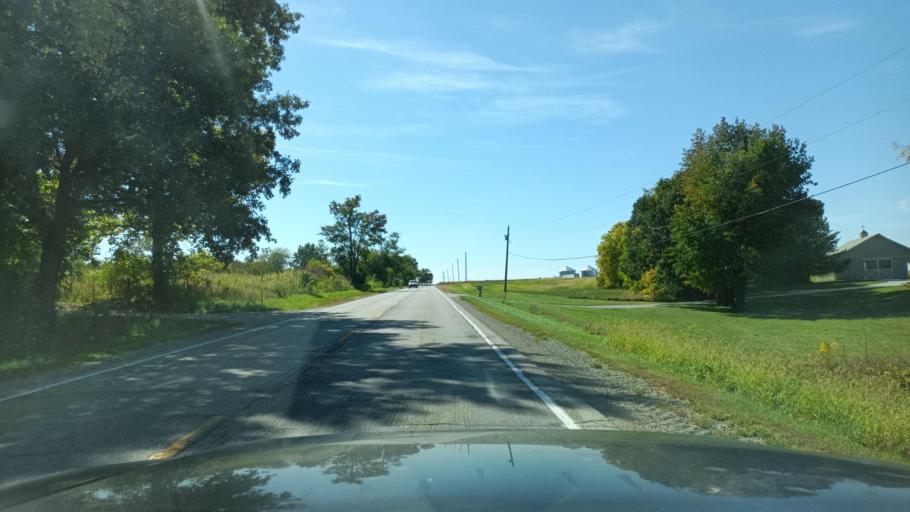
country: US
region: Illinois
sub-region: De Witt County
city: Farmer City
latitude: 40.2267
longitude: -88.6887
